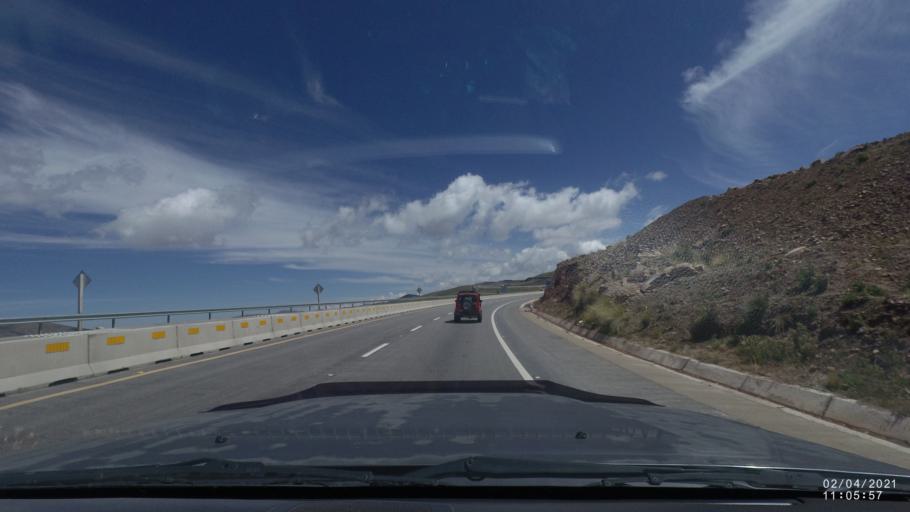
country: BO
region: Cochabamba
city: Colchani
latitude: -17.6542
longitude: -66.8339
